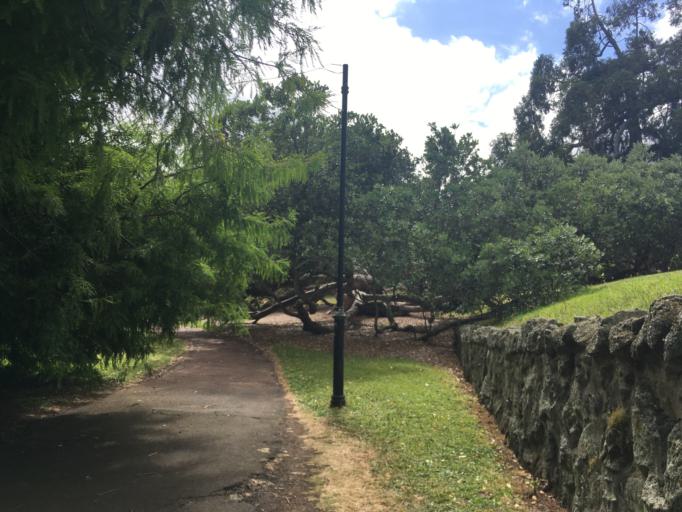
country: NZ
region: Auckland
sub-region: Auckland
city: Auckland
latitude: -36.8600
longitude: 174.7726
